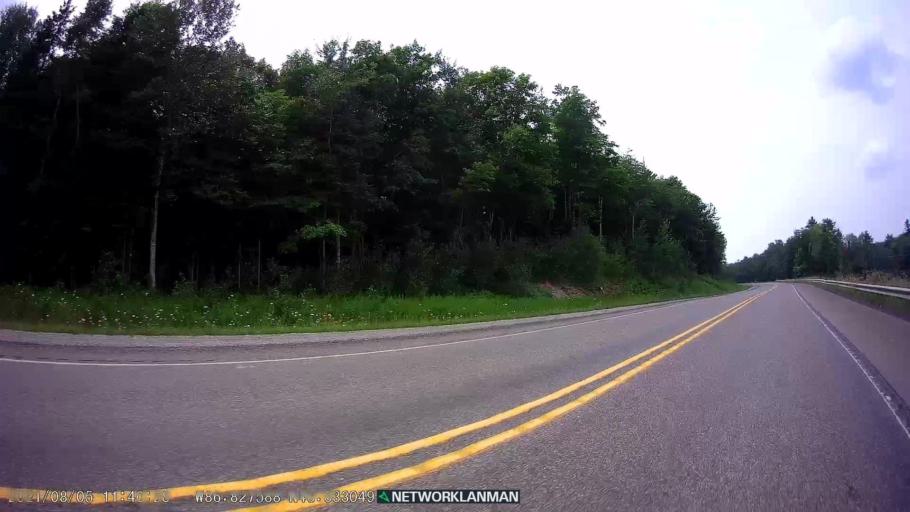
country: US
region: Michigan
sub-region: Alger County
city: Munising
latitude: 46.3333
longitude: -86.8286
